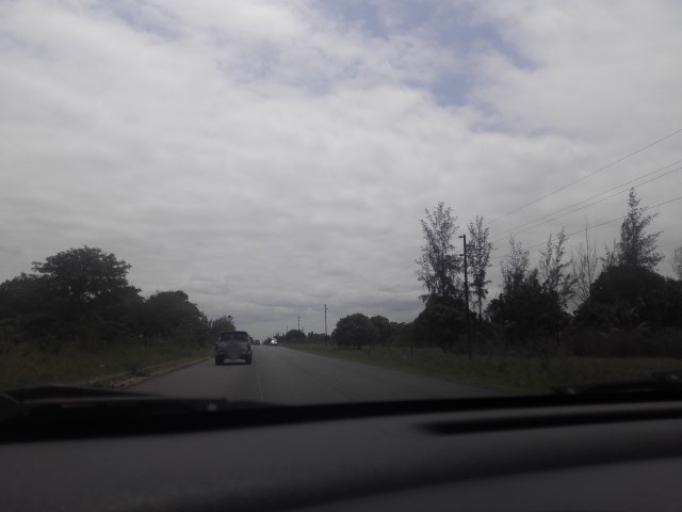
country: MZ
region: Maputo
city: Manhica
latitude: -25.4105
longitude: 32.7593
